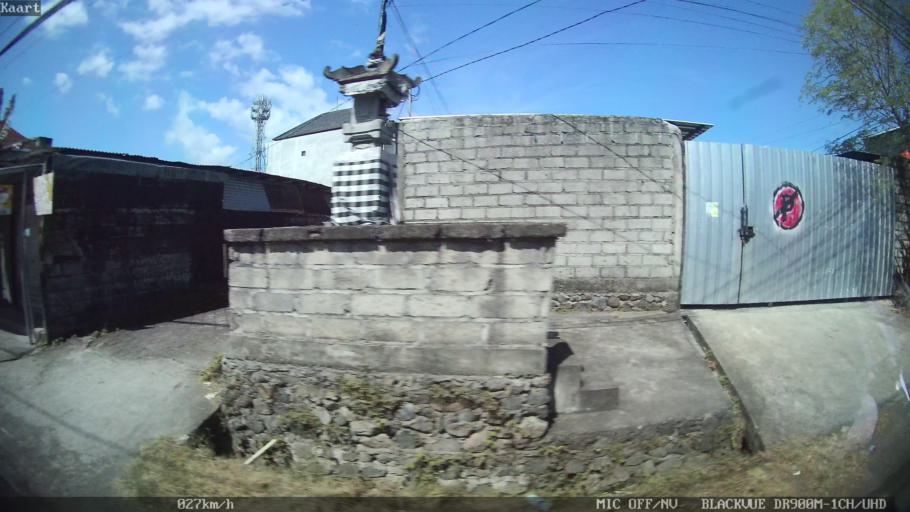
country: ID
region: Bali
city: Denpasar
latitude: -8.6499
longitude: 115.1782
